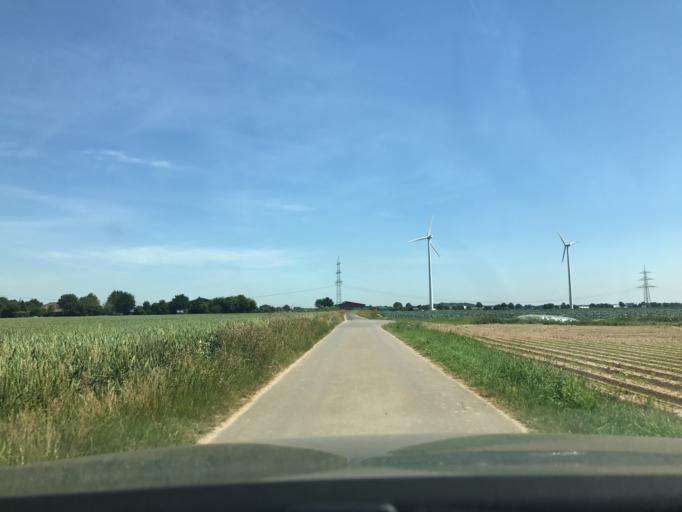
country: DE
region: North Rhine-Westphalia
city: Tonisvorst
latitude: 51.3617
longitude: 6.4863
